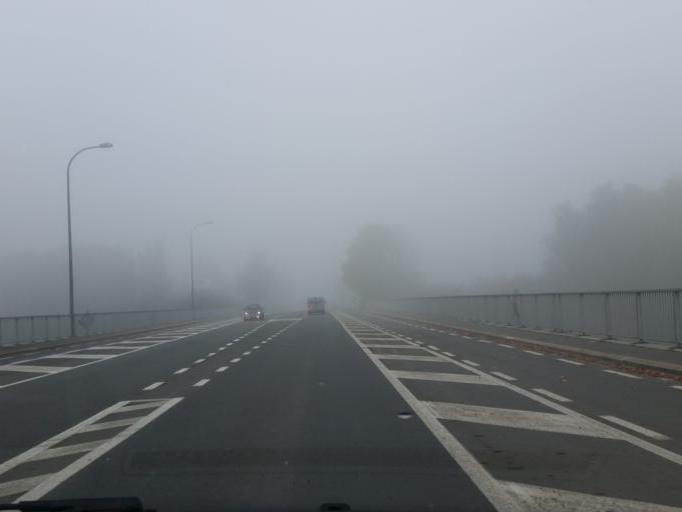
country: BE
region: Flanders
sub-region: Provincie Oost-Vlaanderen
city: Melle
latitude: 51.0072
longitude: 3.7949
